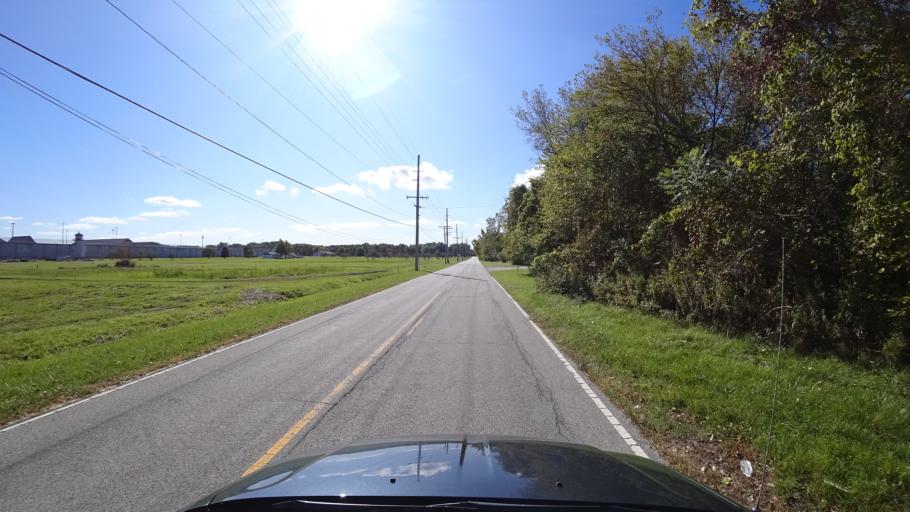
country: US
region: Indiana
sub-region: LaPorte County
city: Michigan City
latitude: 41.7053
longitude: -86.9221
